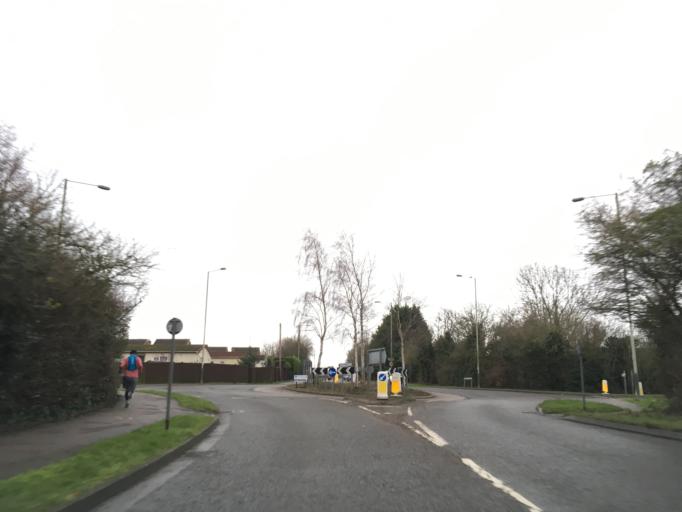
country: GB
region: England
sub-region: Gloucestershire
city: Shurdington
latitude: 51.8880
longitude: -2.1345
